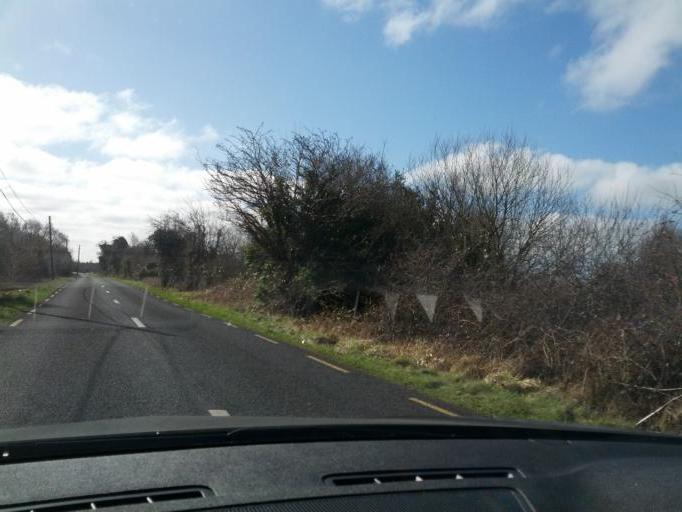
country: IE
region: Connaught
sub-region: County Galway
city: Ballinasloe
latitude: 53.3536
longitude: -8.2550
